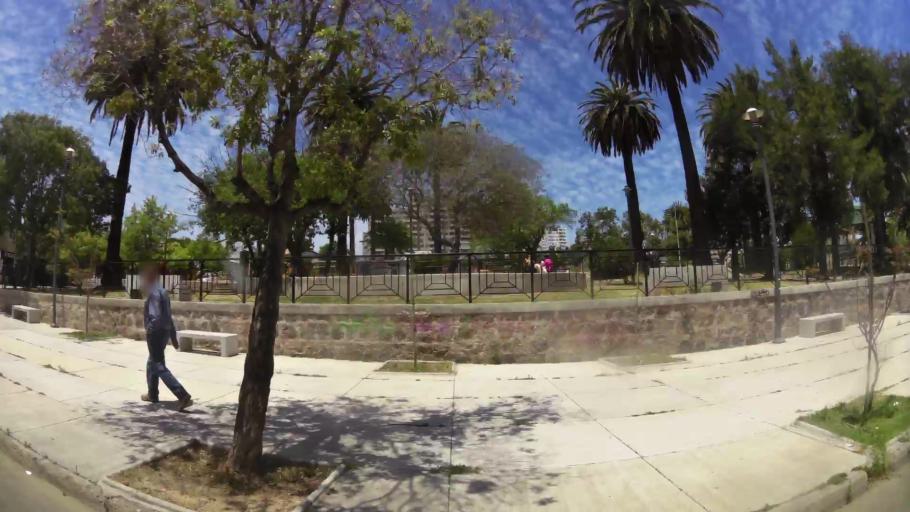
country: CL
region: Valparaiso
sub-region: Provincia de Valparaiso
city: Valparaiso
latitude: -33.0394
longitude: -71.5910
